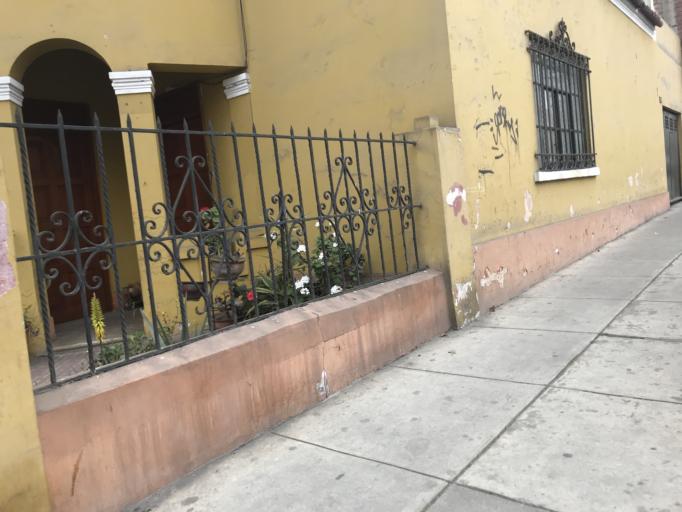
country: PE
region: Lima
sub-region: Lima
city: San Isidro
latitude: -12.0863
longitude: -77.0696
